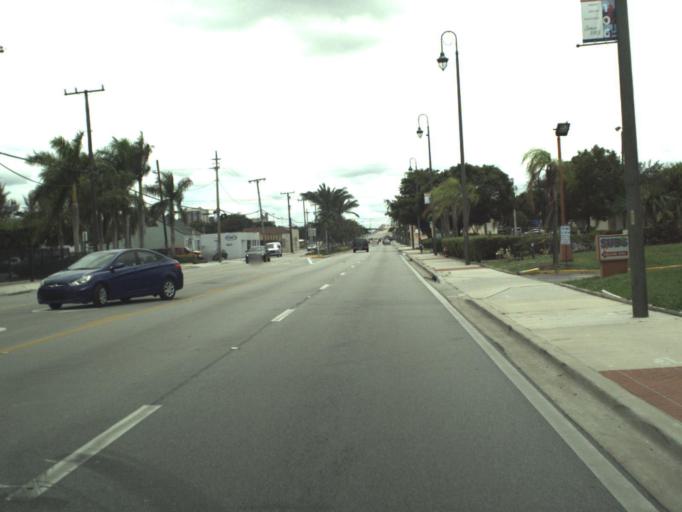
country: US
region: Florida
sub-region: Palm Beach County
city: Riviera Beach
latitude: 26.7781
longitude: -80.0550
